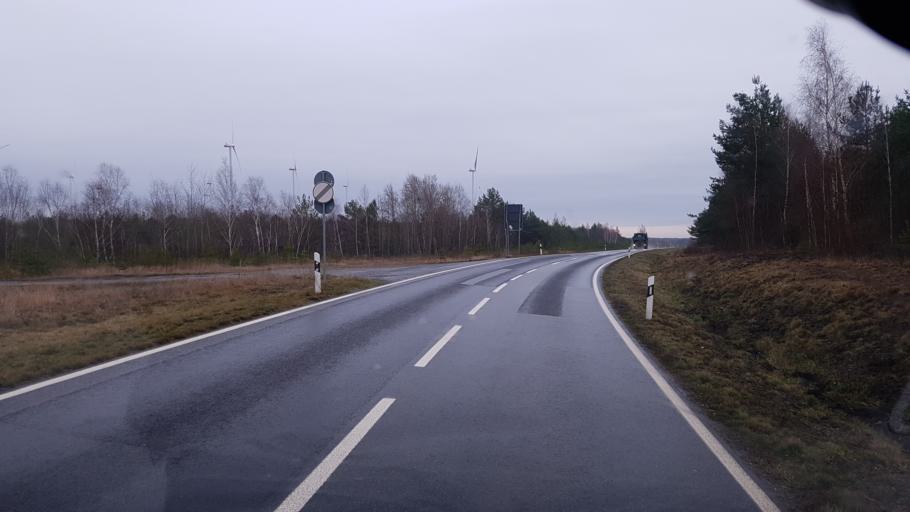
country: DE
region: Brandenburg
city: Schwarzheide
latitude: 51.5167
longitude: 13.8384
